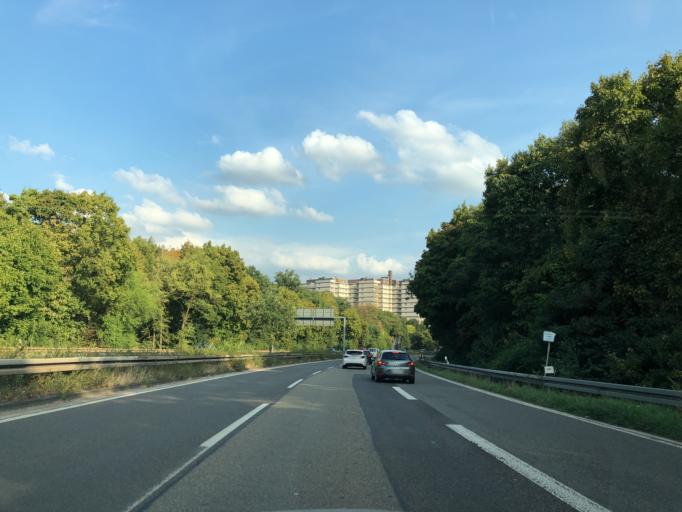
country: DE
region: Hesse
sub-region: Regierungsbezirk Darmstadt
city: Offenbach
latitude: 50.0958
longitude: 8.7426
